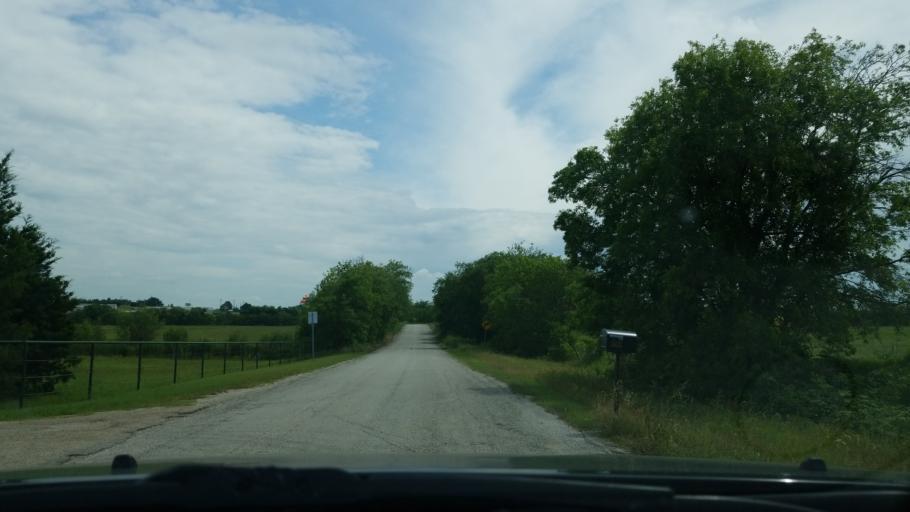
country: US
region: Texas
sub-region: Denton County
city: Sanger
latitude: 33.3052
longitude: -97.1755
